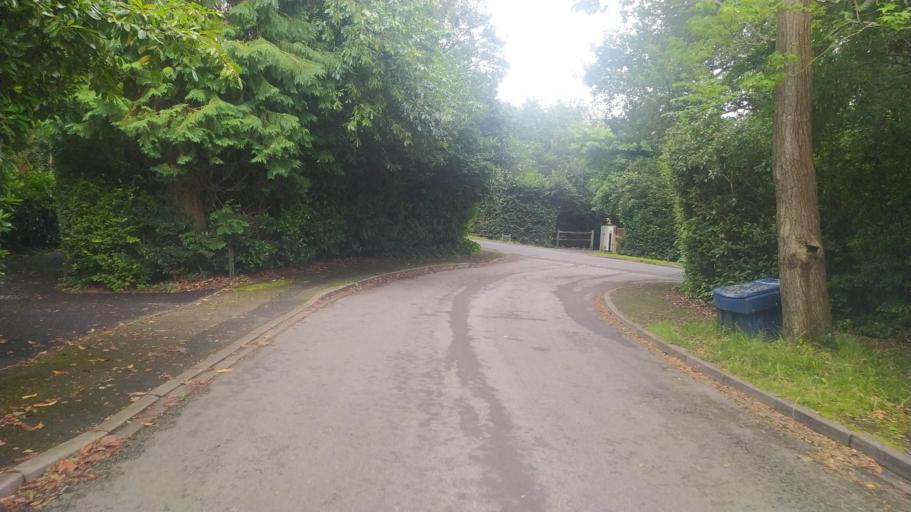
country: GB
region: England
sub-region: Hampshire
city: Liss
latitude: 51.0383
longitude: -0.8856
